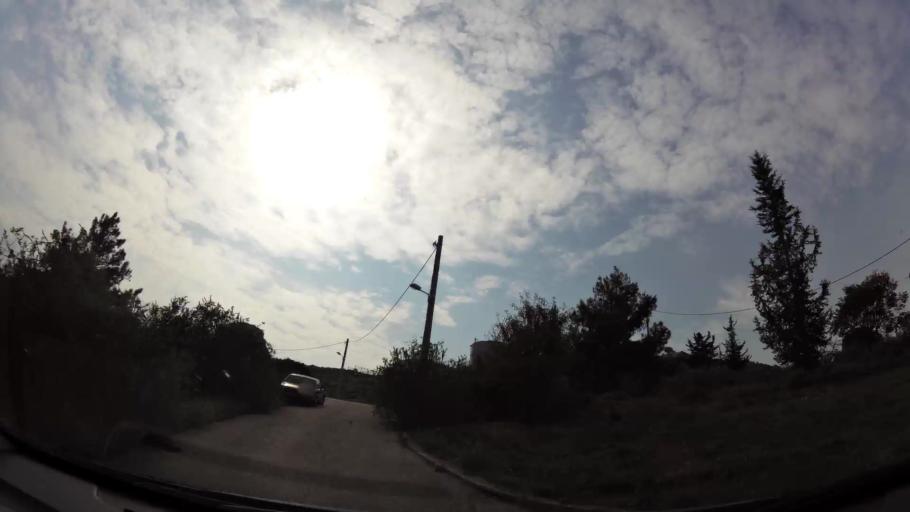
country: GR
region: Attica
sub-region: Nomarchia Athinas
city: Psychiko
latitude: 38.0154
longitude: 23.7635
